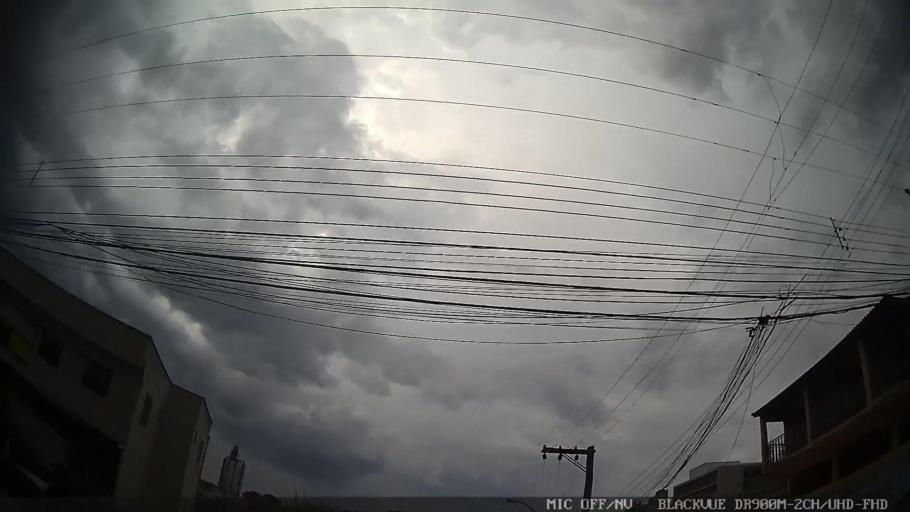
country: BR
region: Sao Paulo
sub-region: Itatiba
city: Itatiba
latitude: -23.0085
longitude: -46.8340
